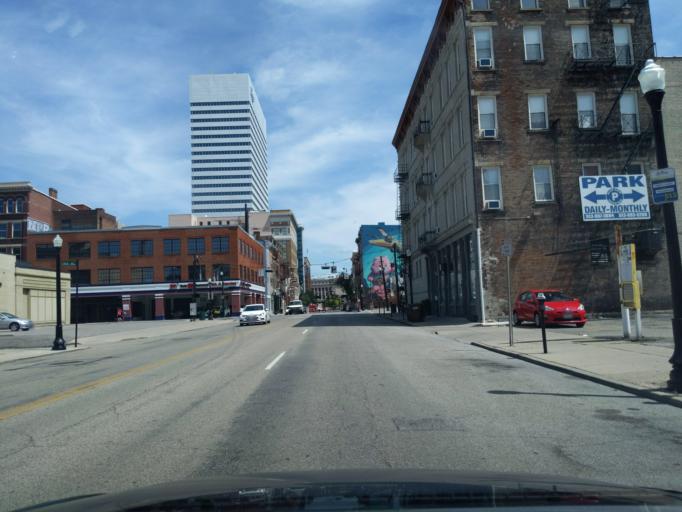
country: US
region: Kentucky
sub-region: Kenton County
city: Covington
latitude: 39.1059
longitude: -84.5166
